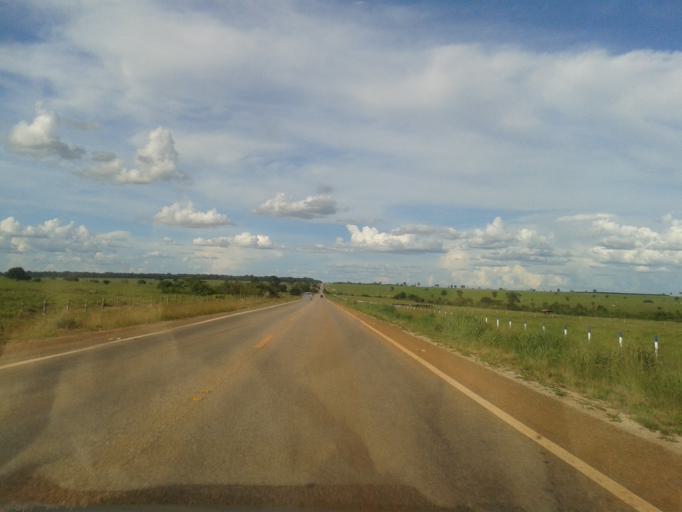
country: BR
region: Goias
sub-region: Mozarlandia
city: Mozarlandia
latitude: -14.3567
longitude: -50.4248
